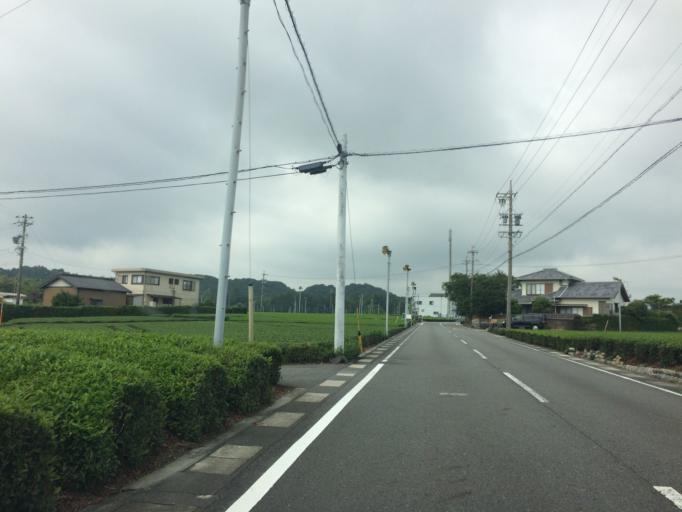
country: JP
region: Shizuoka
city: Shimada
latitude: 34.7987
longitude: 138.2152
